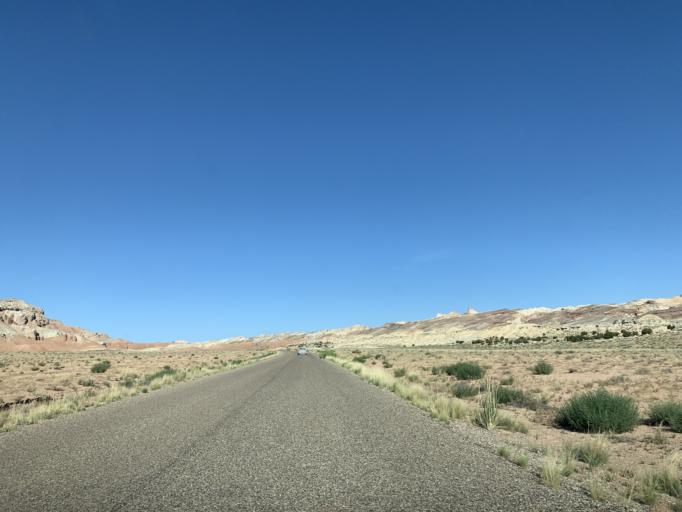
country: US
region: Utah
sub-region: Emery County
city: Ferron
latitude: 38.5784
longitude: -110.7642
